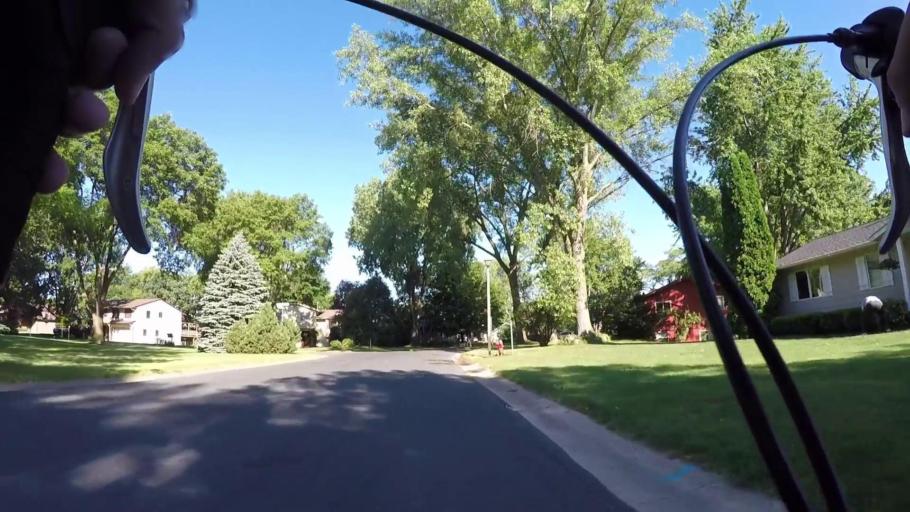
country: US
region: Minnesota
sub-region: Carver County
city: Chanhassen
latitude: 44.8752
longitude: -93.5075
